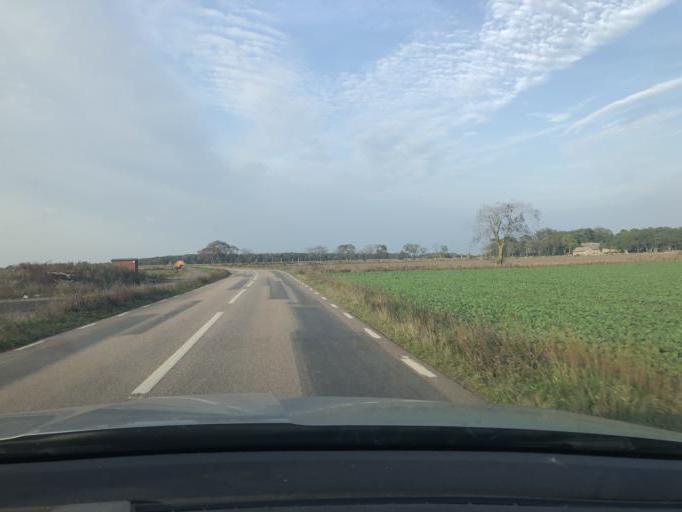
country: SE
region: Kalmar
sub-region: Morbylanga Kommun
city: Moerbylanga
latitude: 56.3007
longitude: 16.4102
